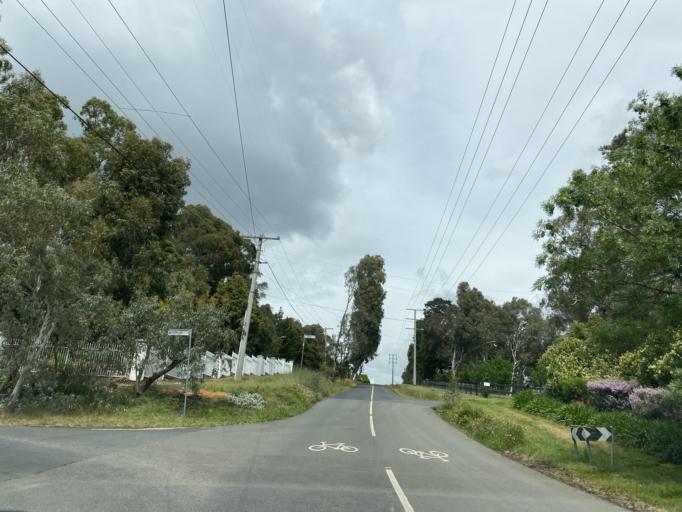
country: AU
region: Victoria
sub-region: Banyule
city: Darch
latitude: -37.7438
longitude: 145.1145
